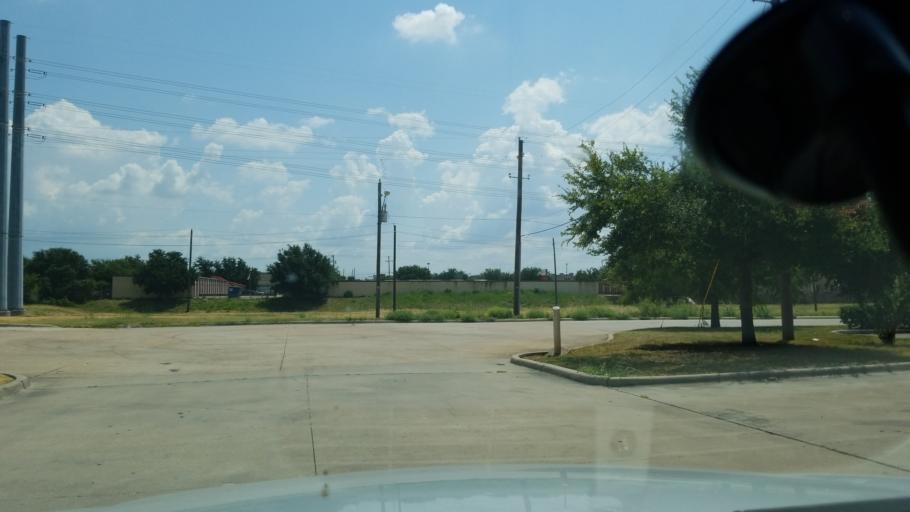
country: US
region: Texas
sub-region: Dallas County
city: Farmers Branch
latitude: 32.8639
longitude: -96.8929
